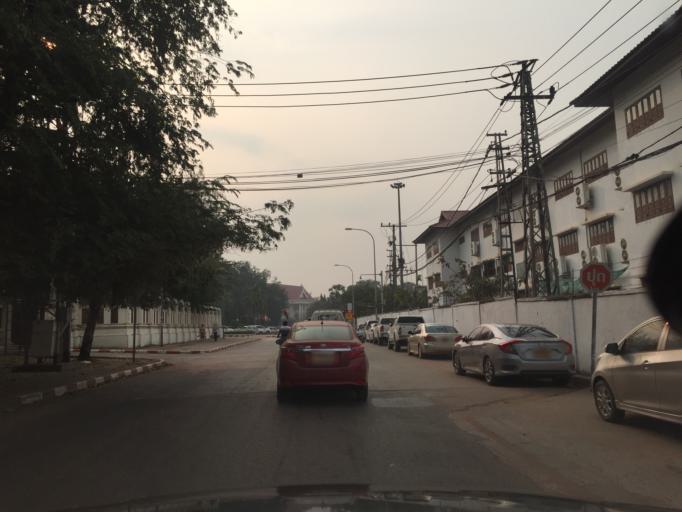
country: LA
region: Vientiane
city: Vientiane
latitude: 17.9710
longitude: 102.6171
